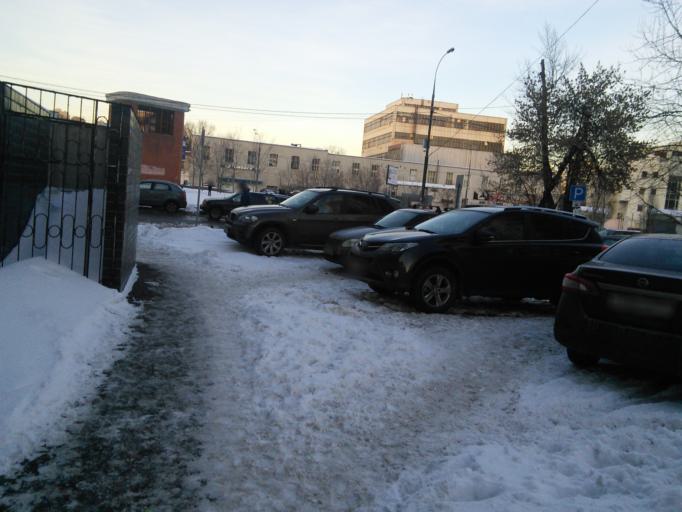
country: RU
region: Moscow
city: Lefortovo
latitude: 55.7704
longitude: 37.6886
